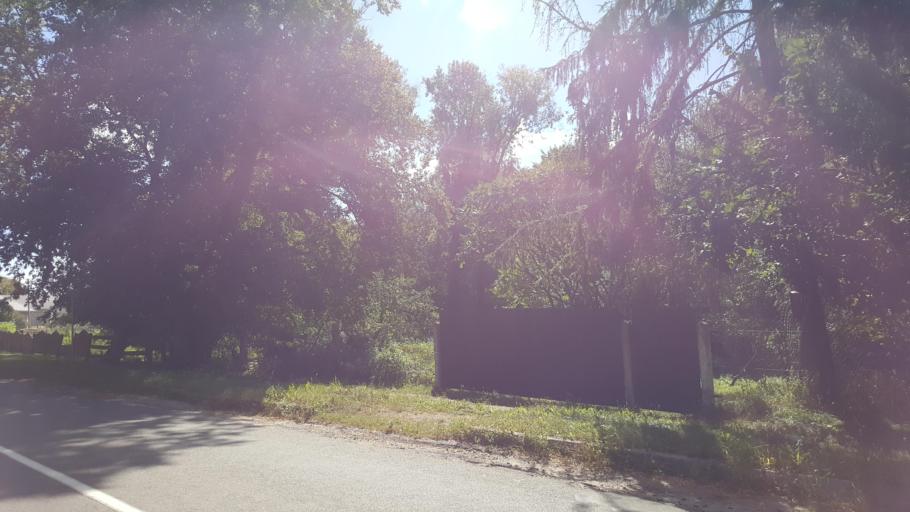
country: BY
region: Brest
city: Vysokaye
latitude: 52.2855
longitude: 23.3103
